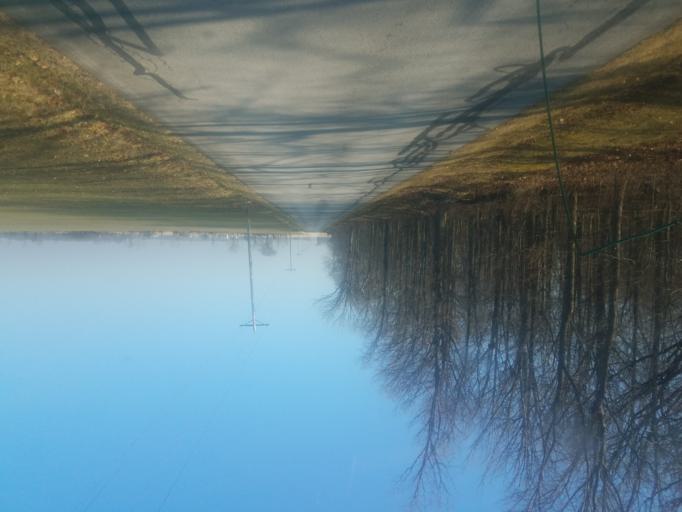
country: US
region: Ohio
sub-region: Seneca County
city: Tiffin
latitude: 41.0371
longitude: -83.1007
